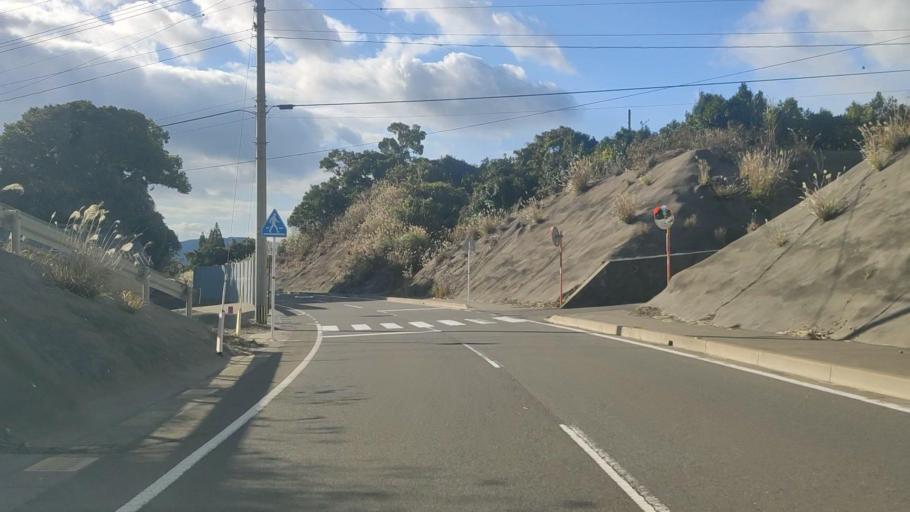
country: JP
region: Kagoshima
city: Tarumizu
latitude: 31.5972
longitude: 130.7079
